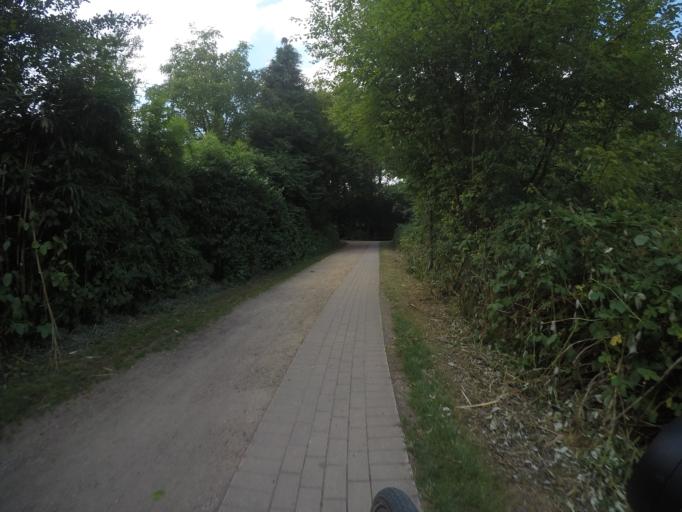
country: DE
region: Hamburg
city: Bergedorf
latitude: 53.5016
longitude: 10.2070
